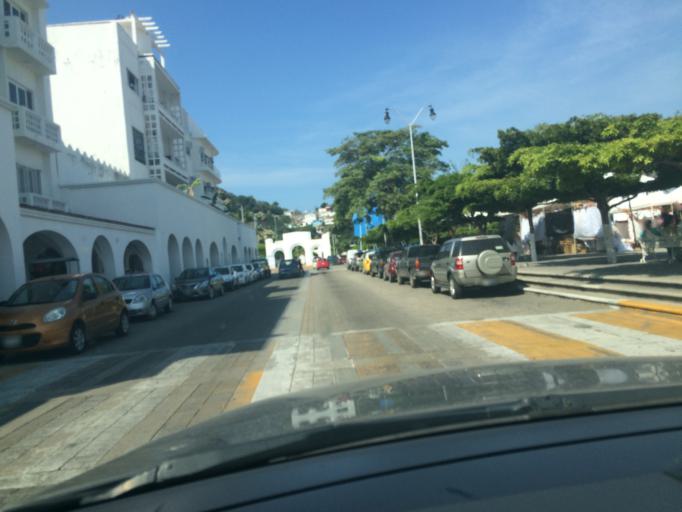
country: MX
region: Colima
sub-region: Manzanillo
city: Manzanillo
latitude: 19.0537
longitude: -104.3153
